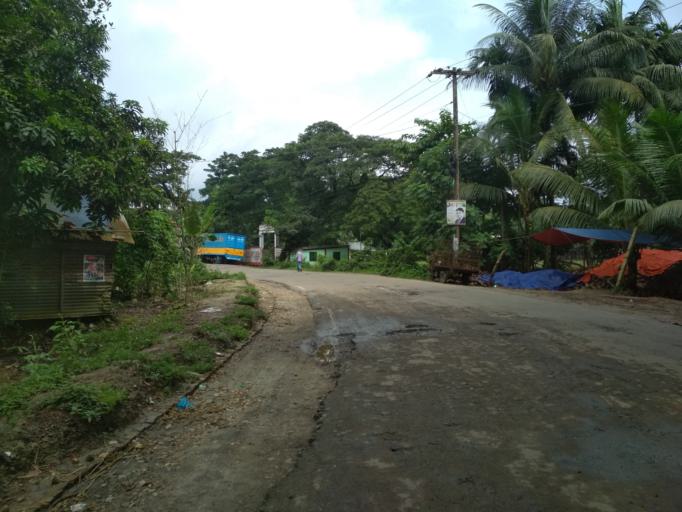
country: BD
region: Chittagong
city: Lakshmipur
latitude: 22.9679
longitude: 90.8096
